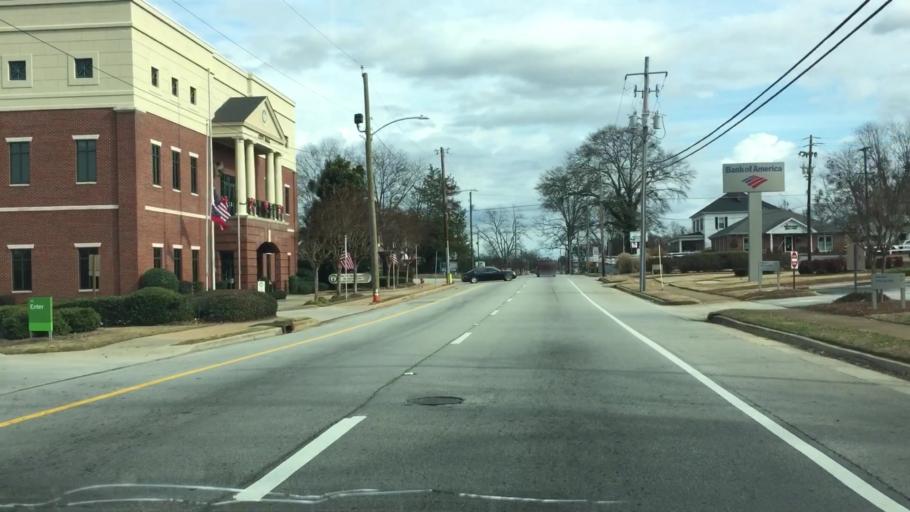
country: US
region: Georgia
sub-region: Henry County
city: McDonough
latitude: 33.4470
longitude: -84.1431
